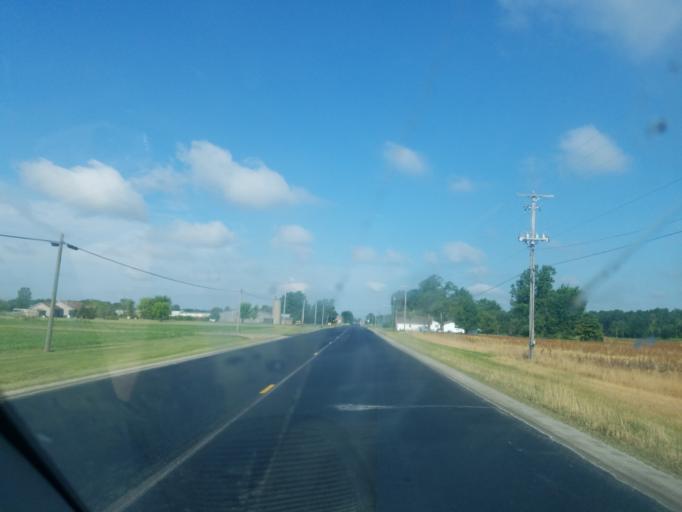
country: US
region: Ohio
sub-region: Allen County
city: Lima
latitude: 40.7314
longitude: -83.9799
